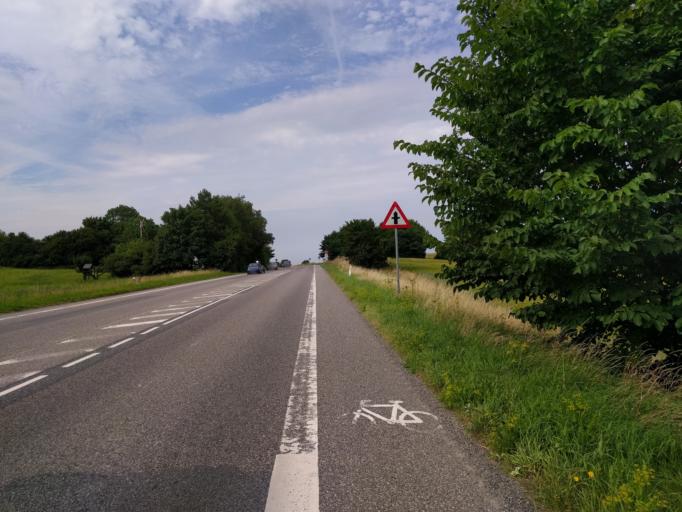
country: DK
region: Zealand
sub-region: Kalundborg Kommune
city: Svebolle
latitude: 55.7026
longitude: 11.3436
